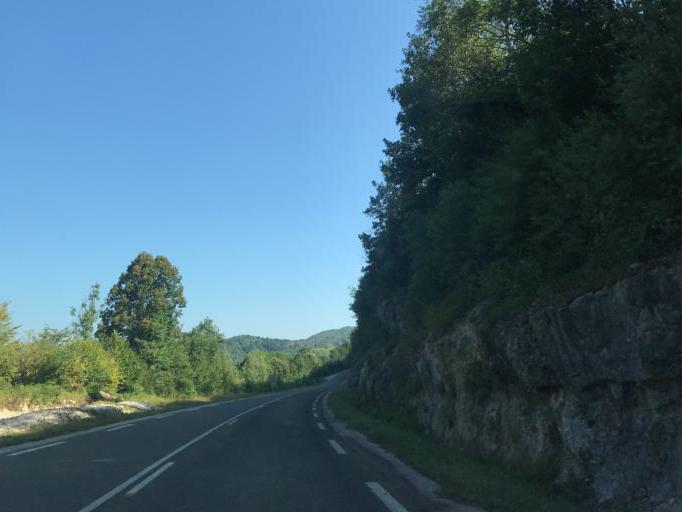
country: FR
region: Franche-Comte
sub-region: Departement du Jura
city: Moirans-en-Montagne
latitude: 46.3993
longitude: 5.7338
